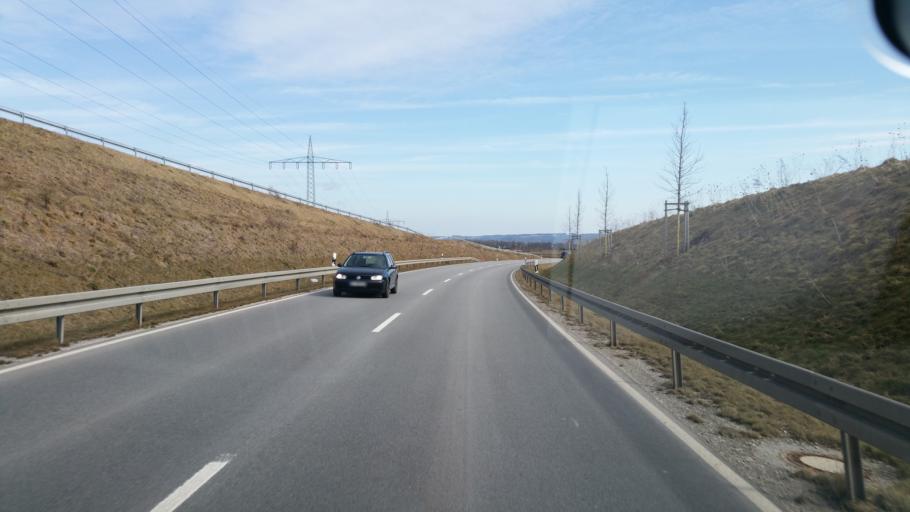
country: DE
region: Bavaria
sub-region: Lower Bavaria
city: Ergolding
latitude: 48.5667
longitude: 12.1142
